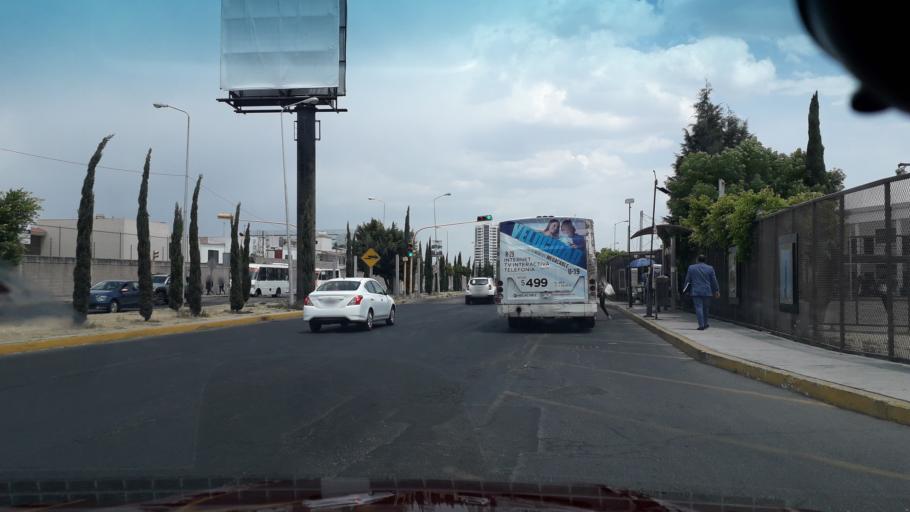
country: MX
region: Puebla
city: Tlazcalancingo
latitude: 19.0220
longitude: -98.2411
